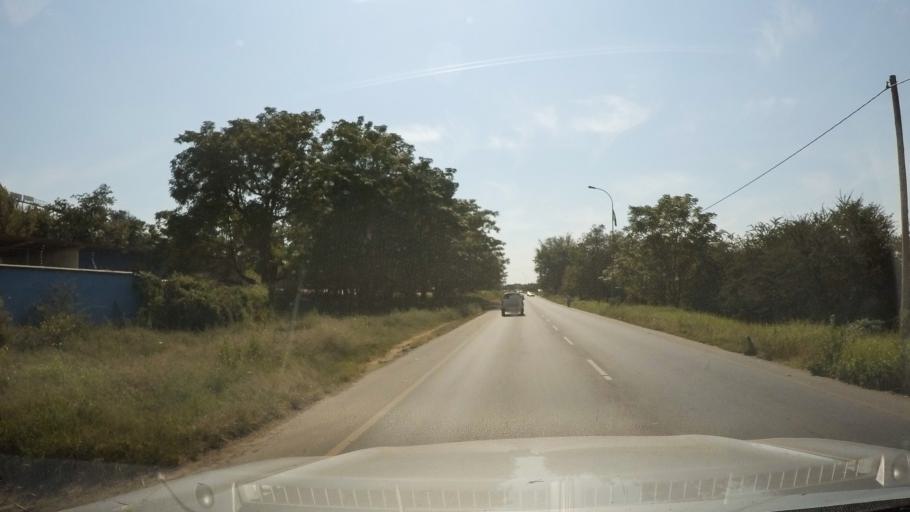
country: BW
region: South East
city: Lobatse
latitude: -25.2237
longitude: 25.6781
